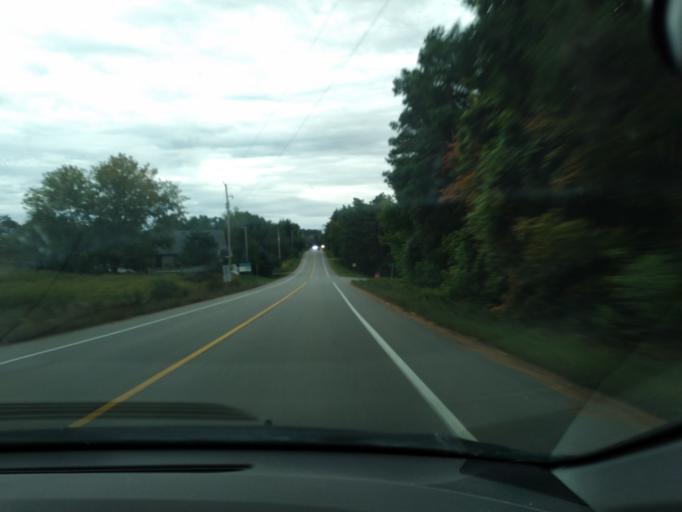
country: CA
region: Ontario
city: Bradford West Gwillimbury
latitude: 43.9770
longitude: -79.8008
